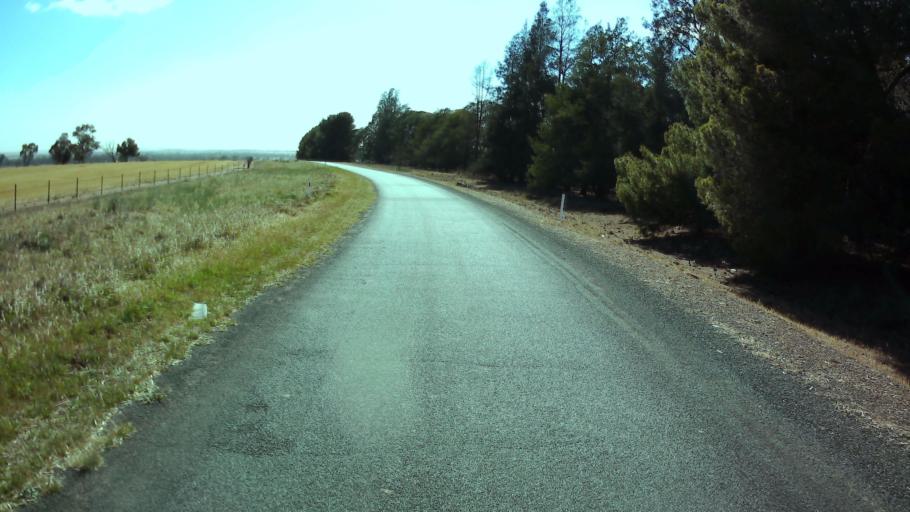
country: AU
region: New South Wales
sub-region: Weddin
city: Grenfell
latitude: -34.0627
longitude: 148.2639
